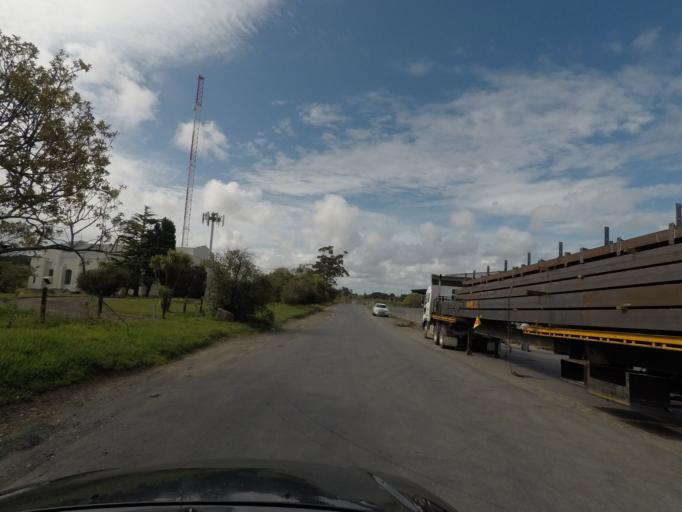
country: NZ
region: Auckland
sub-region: Auckland
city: Rosebank
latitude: -36.8461
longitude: 174.6314
